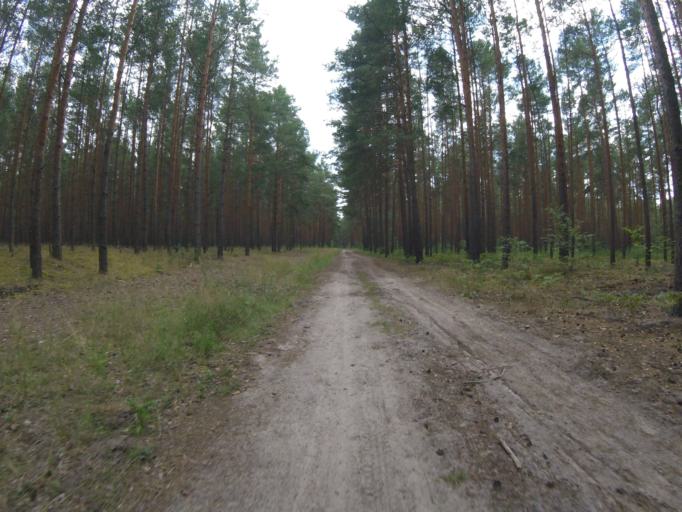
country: DE
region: Brandenburg
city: Halbe
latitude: 52.1357
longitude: 13.6957
